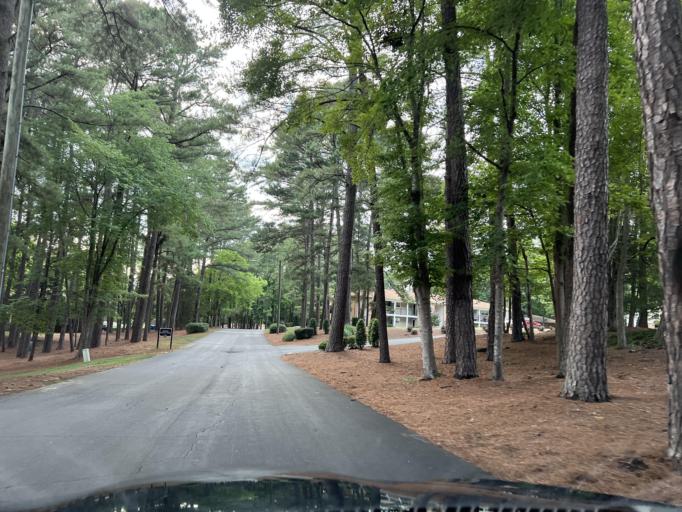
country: US
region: North Carolina
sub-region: Wake County
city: West Raleigh
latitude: 35.8579
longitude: -78.6510
